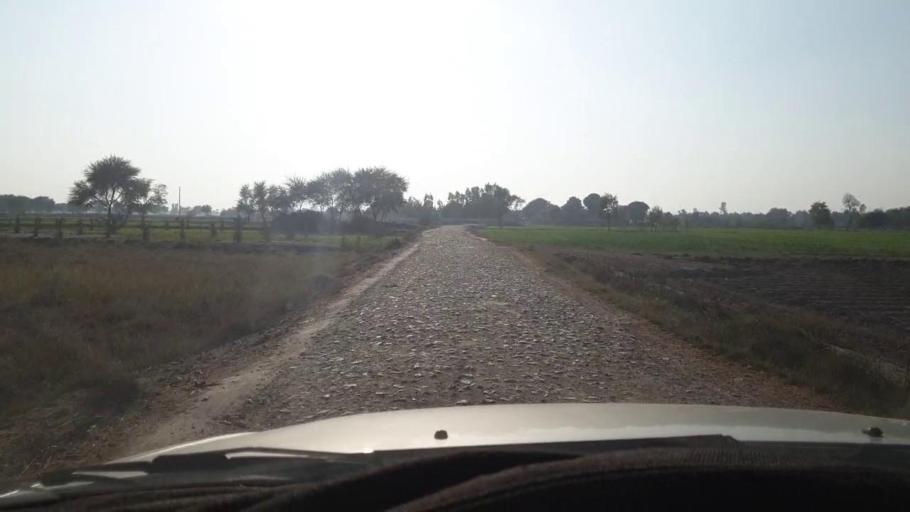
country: PK
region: Sindh
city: Mirpur Mathelo
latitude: 28.0191
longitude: 69.6025
